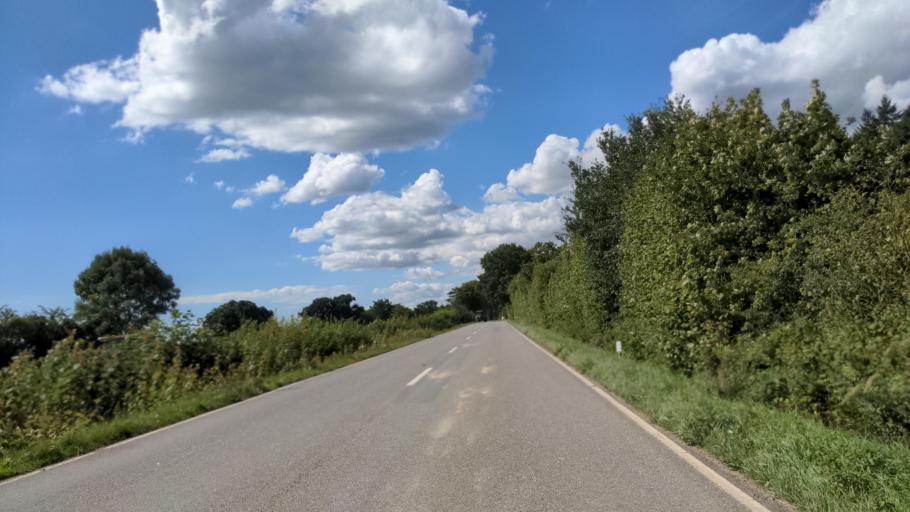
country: DE
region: Schleswig-Holstein
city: Beschendorf
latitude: 54.1993
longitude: 10.8193
